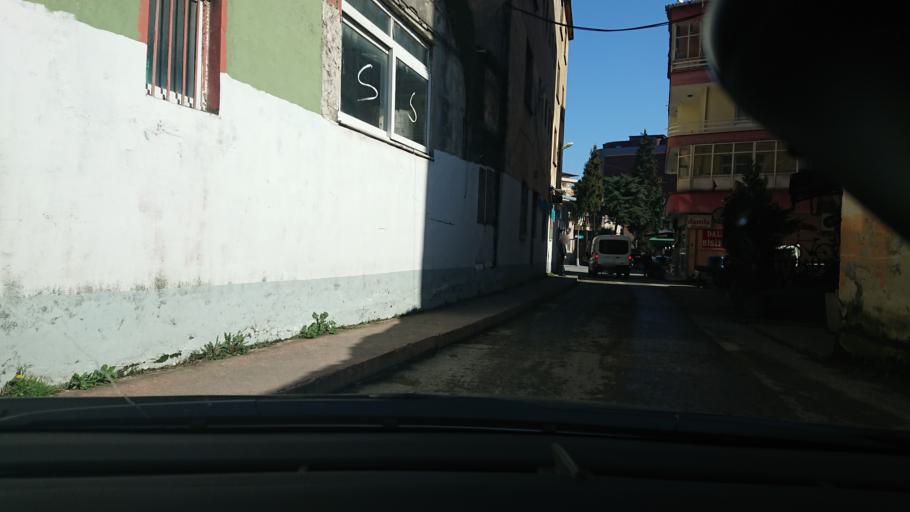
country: TR
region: Rize
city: Rize
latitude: 41.0227
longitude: 40.5262
